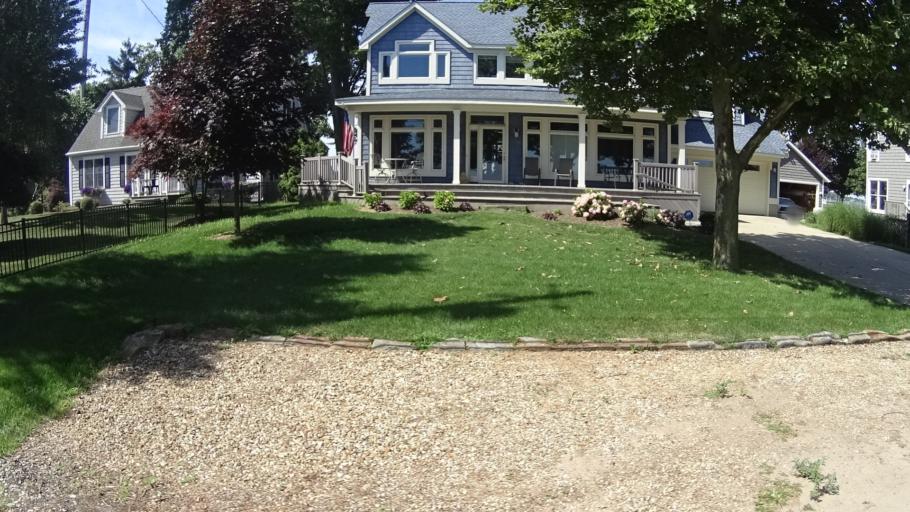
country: US
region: Ohio
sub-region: Erie County
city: Sandusky
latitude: 41.4462
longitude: -82.6402
